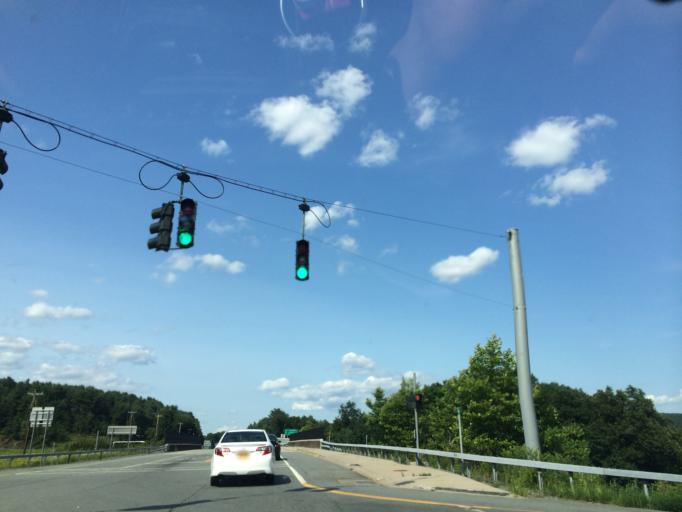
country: US
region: New York
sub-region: Sullivan County
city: Wurtsboro
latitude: 41.5613
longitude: -74.5030
